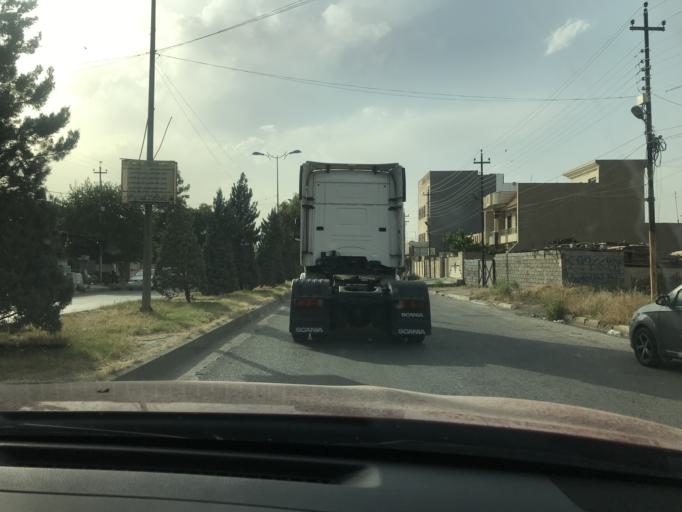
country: IQ
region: Arbil
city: Erbil
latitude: 36.1775
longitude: 43.9806
